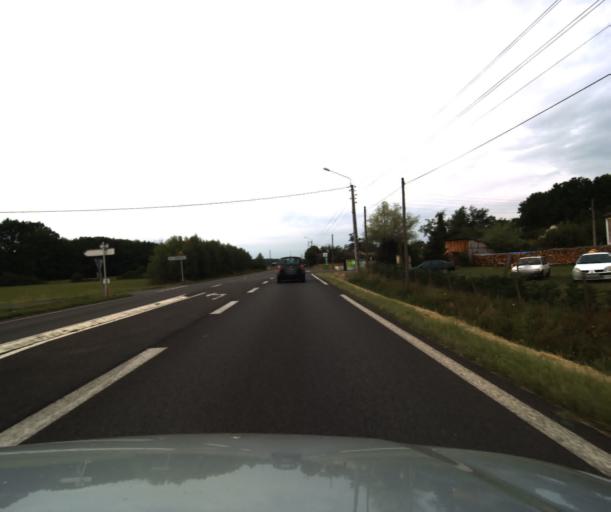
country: FR
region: Midi-Pyrenees
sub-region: Departement des Hautes-Pyrenees
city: Orleix
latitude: 43.3349
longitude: 0.1307
